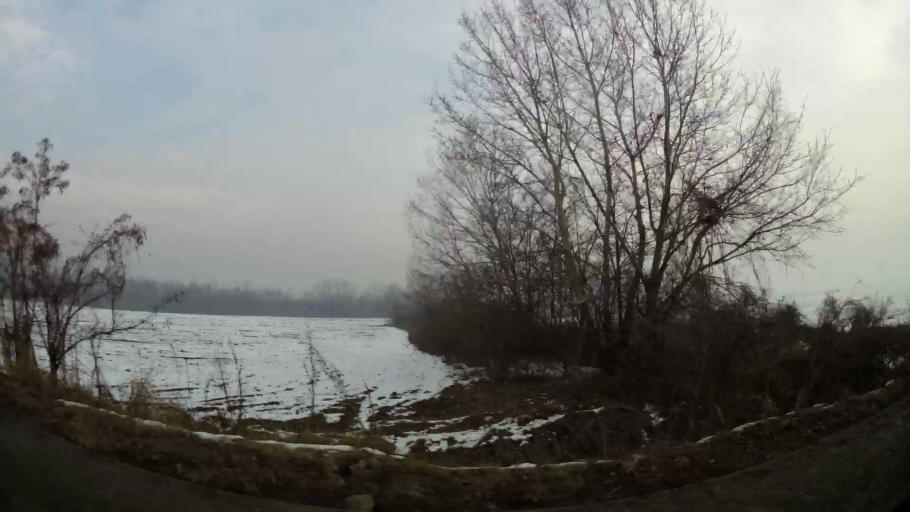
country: MK
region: Kisela Voda
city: Kisela Voda
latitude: 41.9894
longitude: 21.5131
